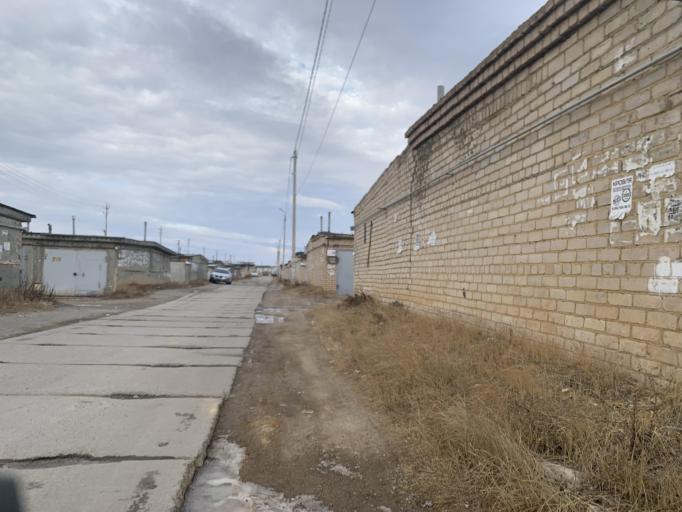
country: RU
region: Chelyabinsk
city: Roshchino
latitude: 55.1859
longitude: 61.2673
